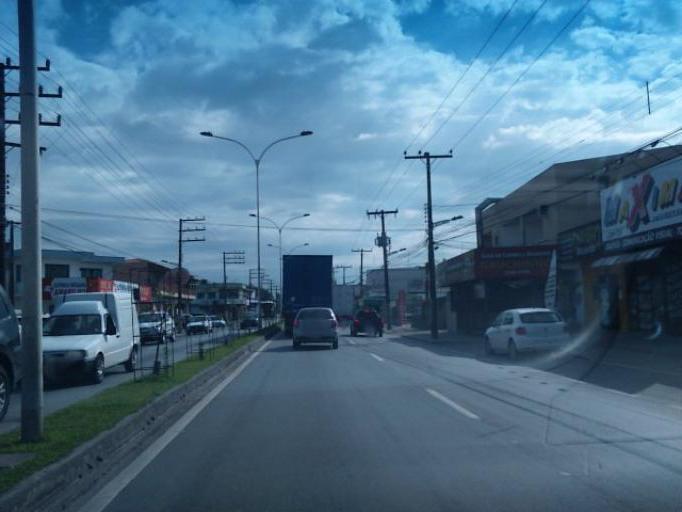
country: BR
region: Santa Catarina
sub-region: Itajai
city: Itajai
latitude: -26.8862
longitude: -48.6978
